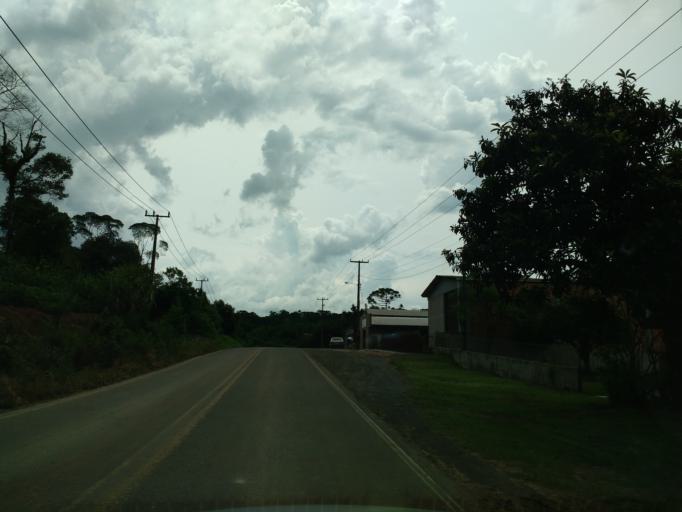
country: BR
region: Parana
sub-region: Prudentopolis
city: Prudentopolis
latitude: -25.1604
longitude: -51.0287
